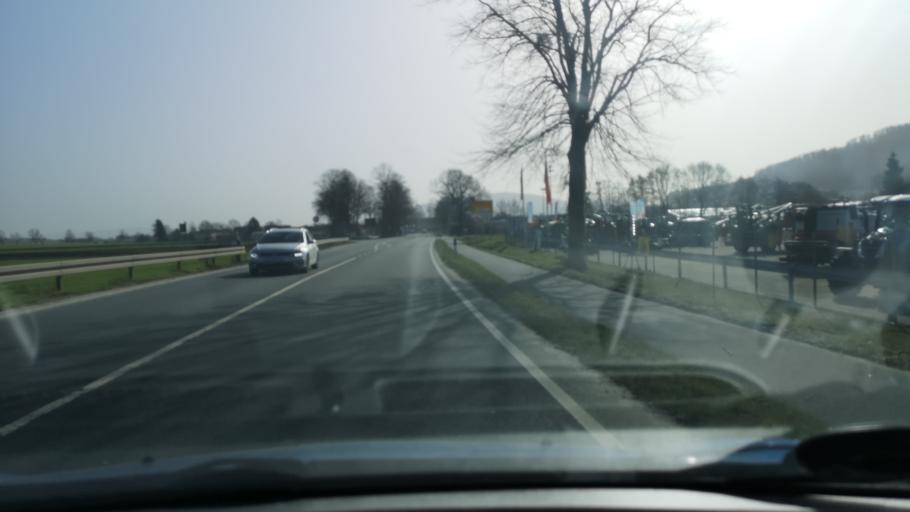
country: DE
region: Lower Saxony
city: Coppenbrugge
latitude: 52.1144
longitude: 9.5594
